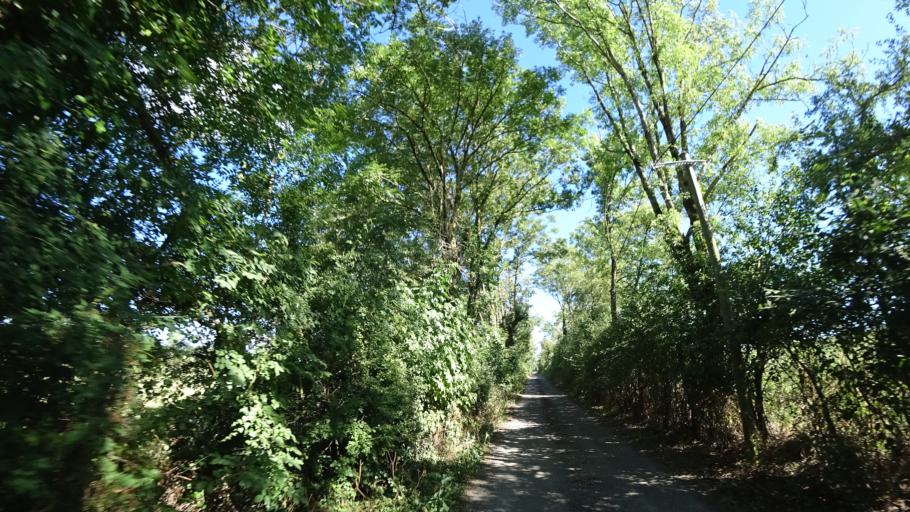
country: FR
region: Midi-Pyrenees
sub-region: Departement de l'Aveyron
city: Druelle
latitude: 44.3885
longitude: 2.5029
